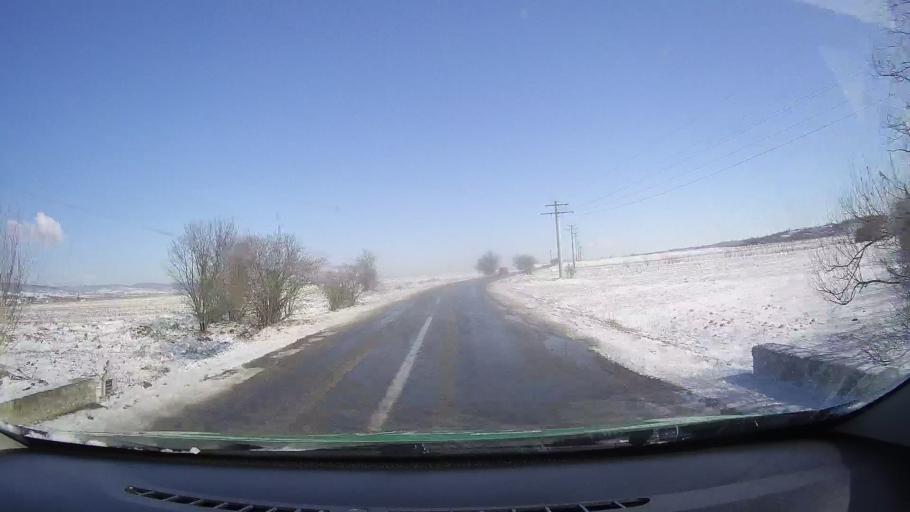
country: RO
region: Sibiu
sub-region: Comuna Racovita
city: Racovita
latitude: 45.6742
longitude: 24.3254
